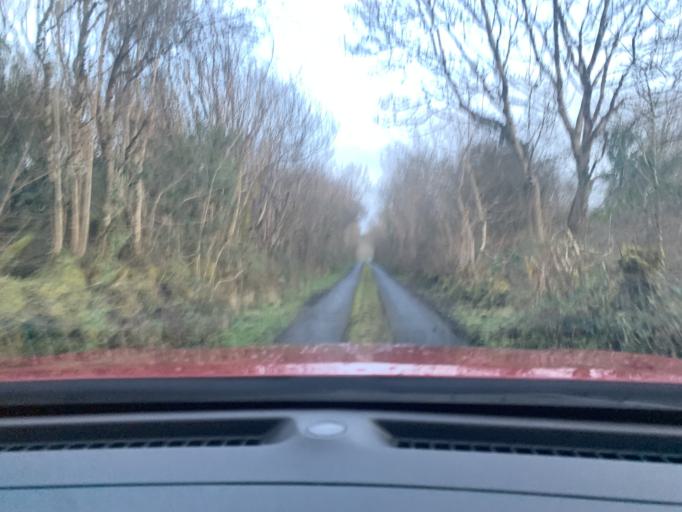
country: IE
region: Connaught
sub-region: Sligo
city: Ballymote
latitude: 53.9908
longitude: -8.4505
